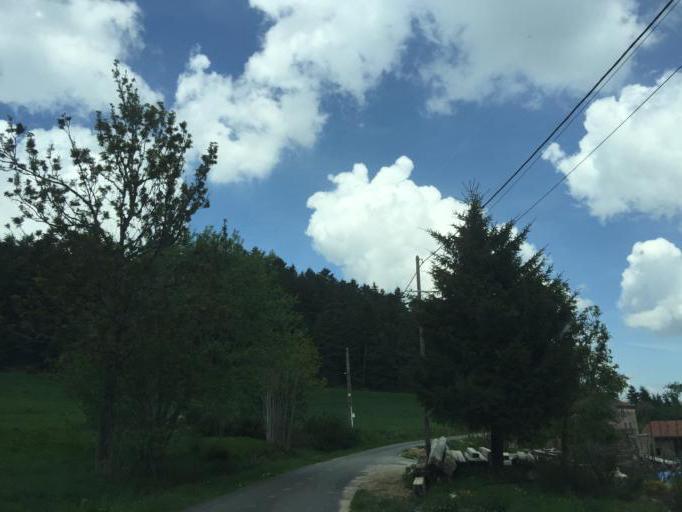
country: FR
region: Rhone-Alpes
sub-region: Departement de la Loire
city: Saint-Sauveur-en-Rue
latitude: 45.2755
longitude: 4.4728
